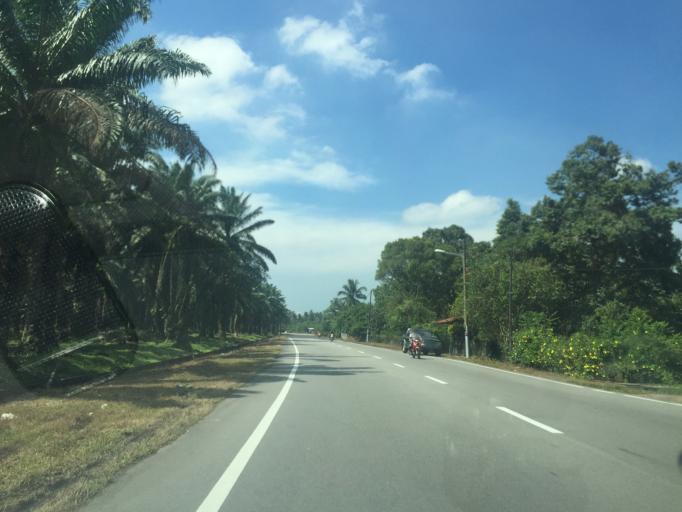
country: MY
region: Penang
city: Tasek Glugor
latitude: 5.4956
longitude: 100.5123
